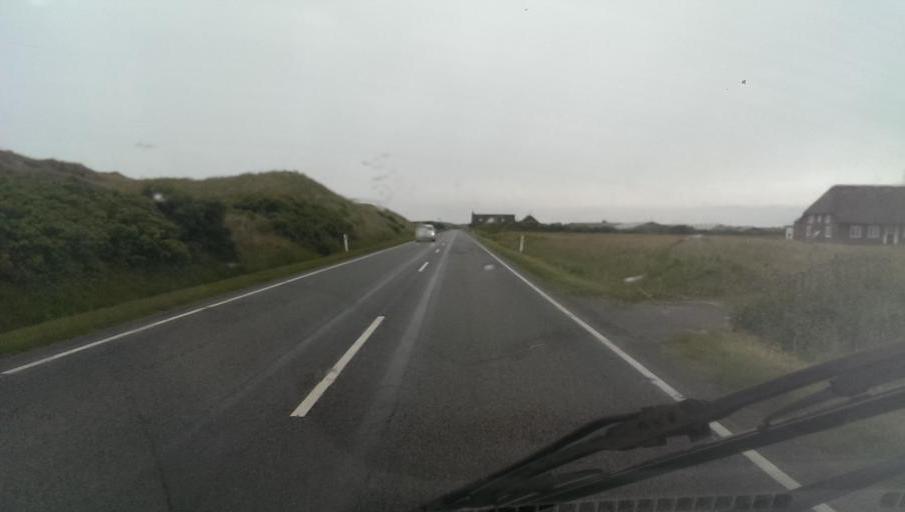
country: DK
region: Central Jutland
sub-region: Ringkobing-Skjern Kommune
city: Hvide Sande
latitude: 55.9723
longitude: 8.1425
